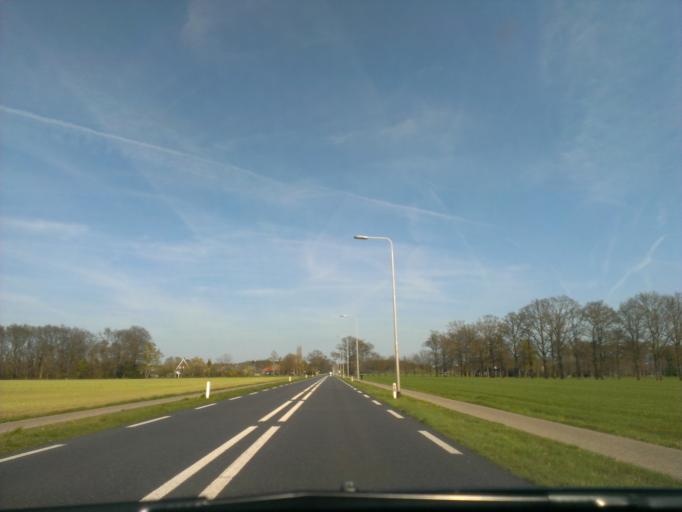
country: NL
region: Gelderland
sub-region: Gemeente Voorst
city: Twello
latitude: 52.2374
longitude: 6.0601
